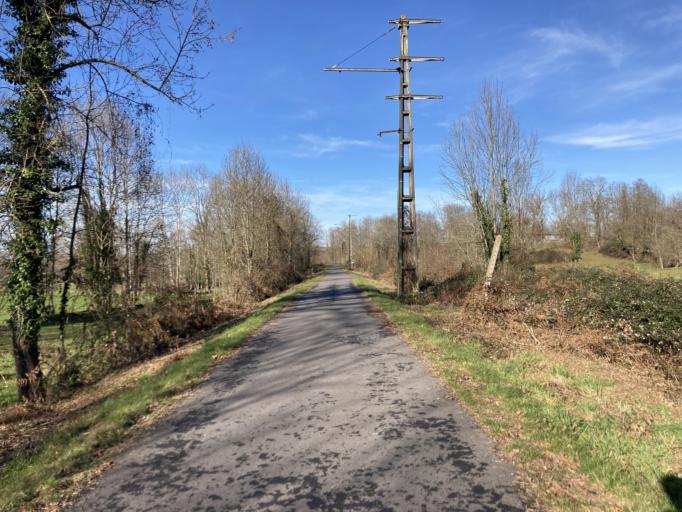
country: FR
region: Aquitaine
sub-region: Departement des Pyrenees-Atlantiques
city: Arudy
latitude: 43.1363
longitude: -0.4469
